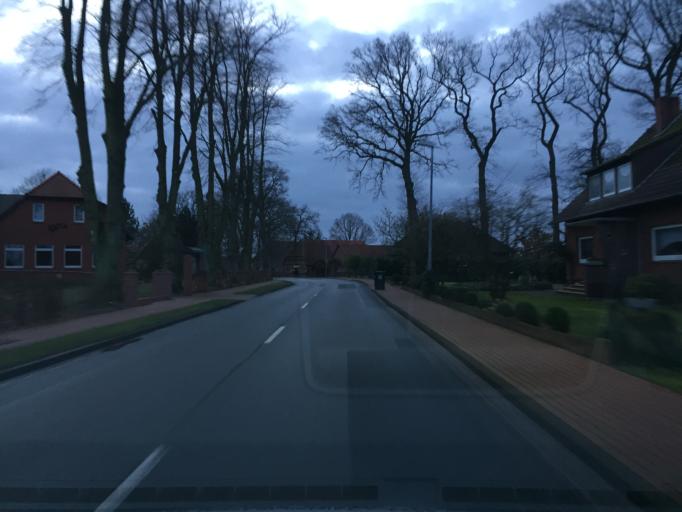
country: DE
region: Lower Saxony
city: Steyerberg
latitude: 52.5933
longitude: 8.9731
